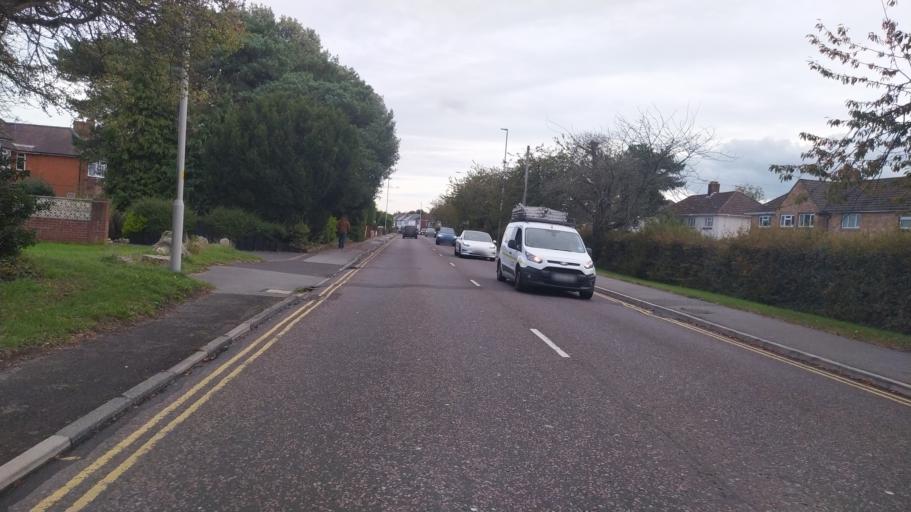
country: GB
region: England
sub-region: Dorset
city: Parkstone
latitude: 50.7489
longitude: -1.9207
